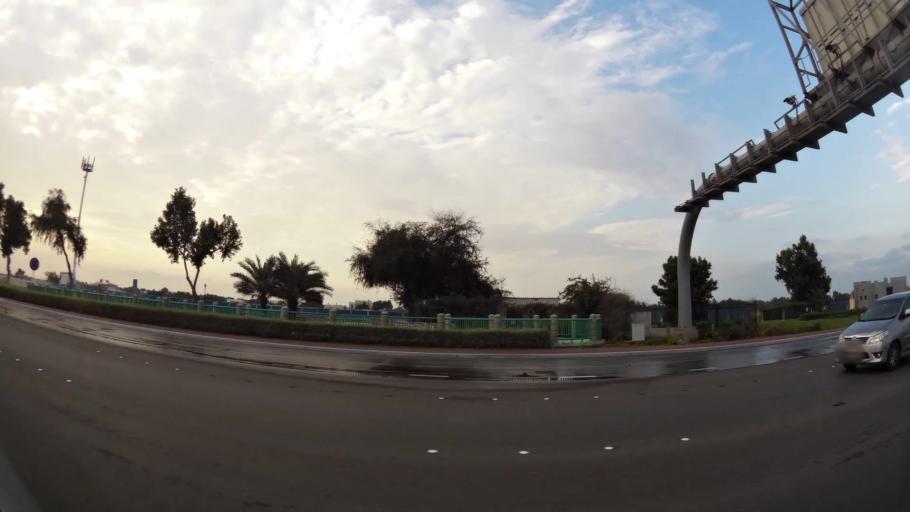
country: AE
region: Abu Dhabi
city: Abu Dhabi
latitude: 24.4194
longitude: 54.4277
